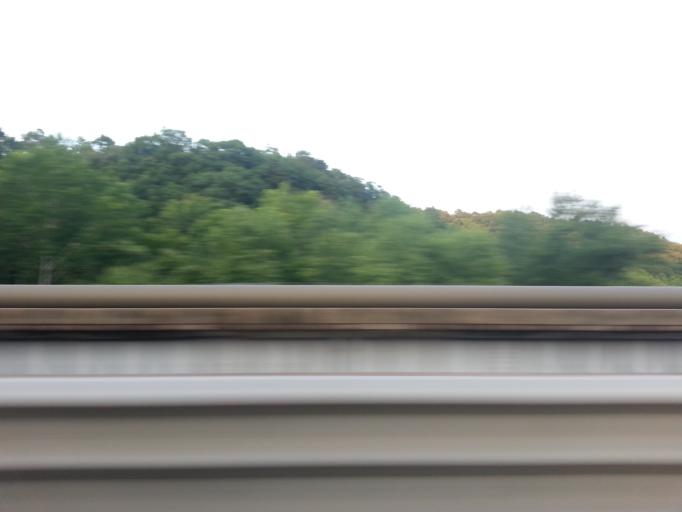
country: US
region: Kentucky
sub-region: Whitley County
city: Williamsburg
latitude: 36.7806
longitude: -84.1703
